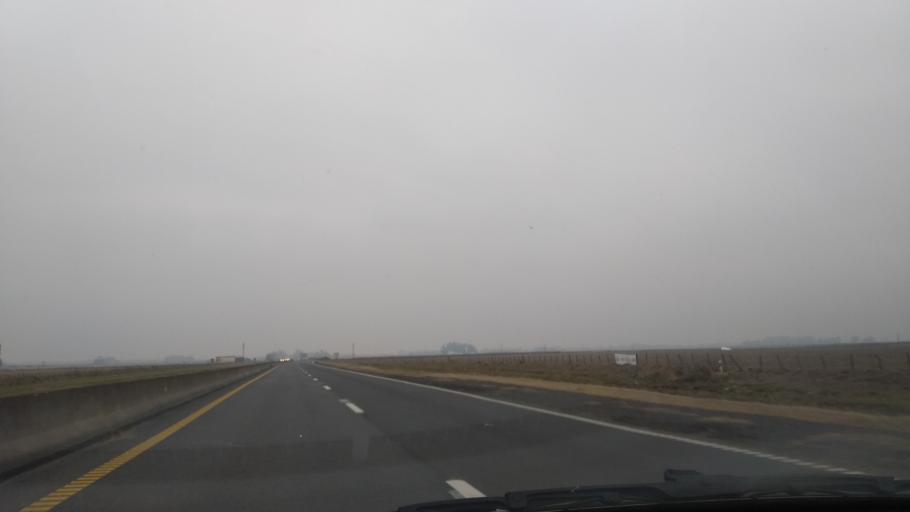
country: AR
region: Buenos Aires
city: Olavarria
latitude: -36.8546
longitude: -60.1138
